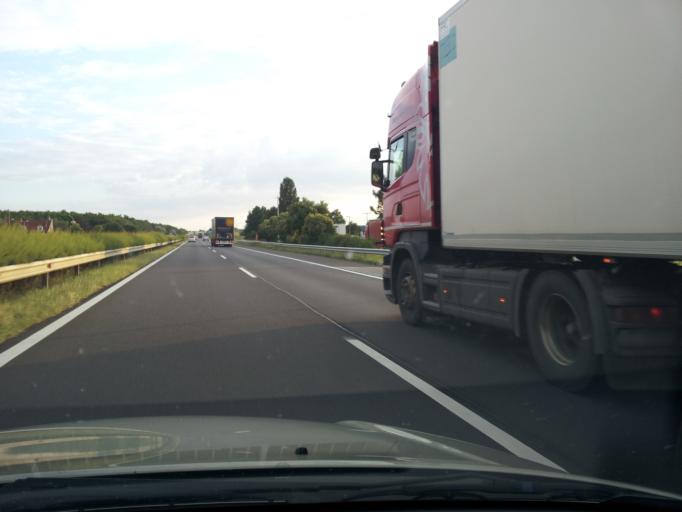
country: HU
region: Heves
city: Hort
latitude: 47.6892
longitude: 19.7436
